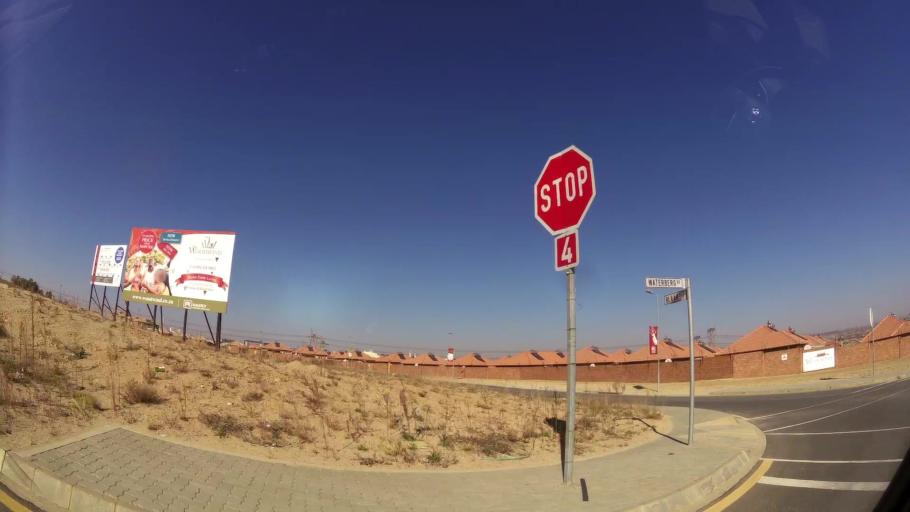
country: ZA
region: Gauteng
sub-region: City of Tshwane Metropolitan Municipality
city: Centurion
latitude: -25.9093
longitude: 28.1256
